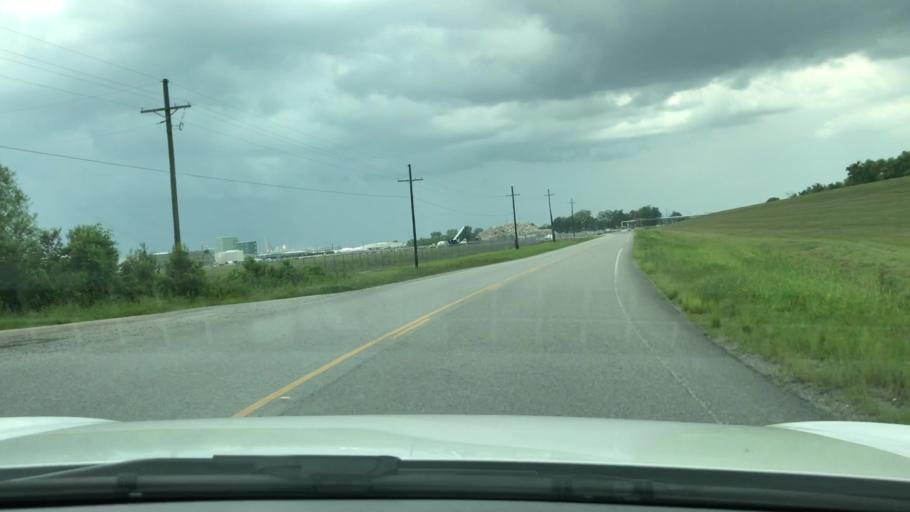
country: US
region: Louisiana
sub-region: Iberville Parish
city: Saint Gabriel
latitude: 30.2737
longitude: -91.1629
